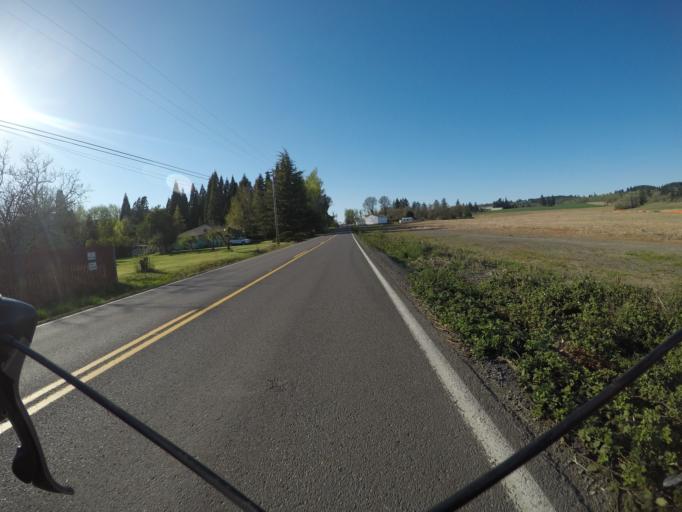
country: US
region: Oregon
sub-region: Washington County
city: Aloha
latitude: 45.4266
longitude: -122.8732
